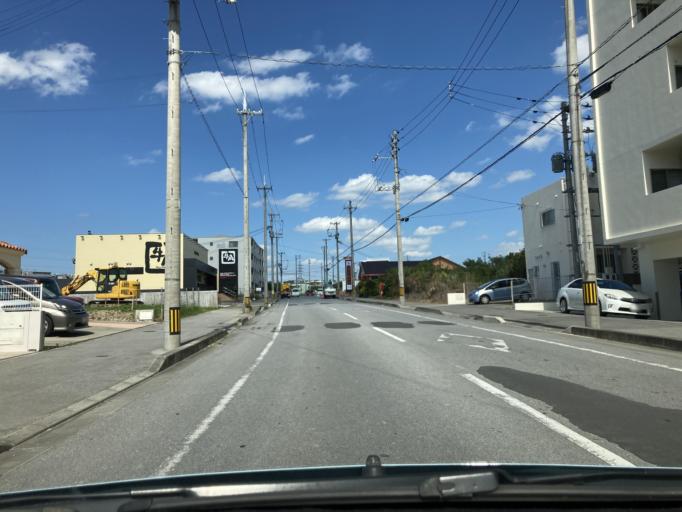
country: JP
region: Okinawa
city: Tomigusuku
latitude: 26.1885
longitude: 127.7106
